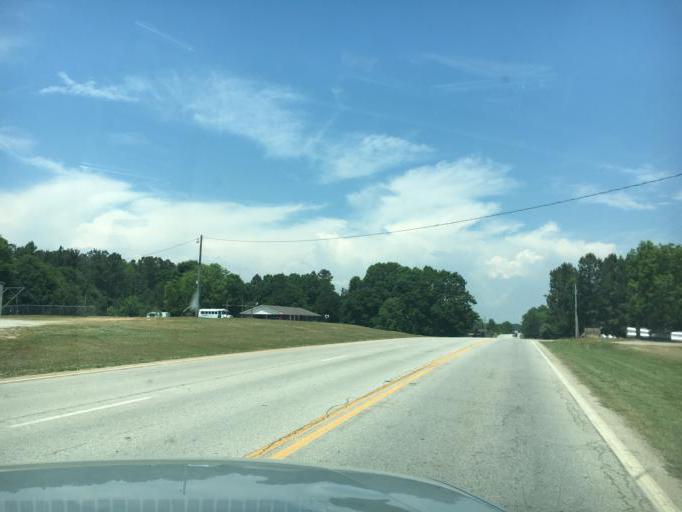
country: US
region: Georgia
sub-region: Hart County
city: Royston
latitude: 34.3194
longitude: -83.1107
